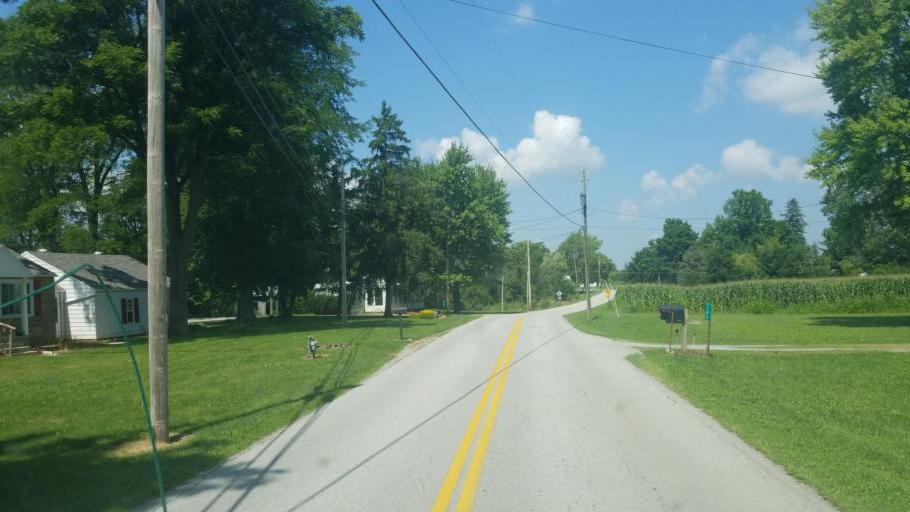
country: US
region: Ohio
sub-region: Allen County
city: Lima
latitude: 40.6930
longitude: -83.9722
